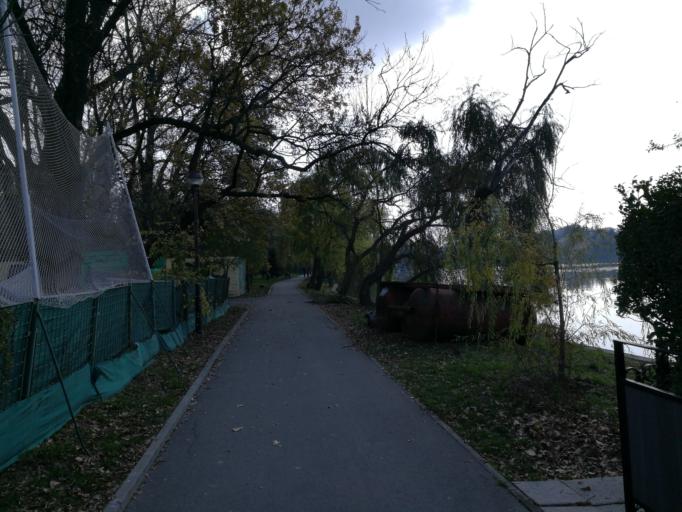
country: RO
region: Bucuresti
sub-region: Municipiul Bucuresti
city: Bucuresti
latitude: 44.4794
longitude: 26.0784
